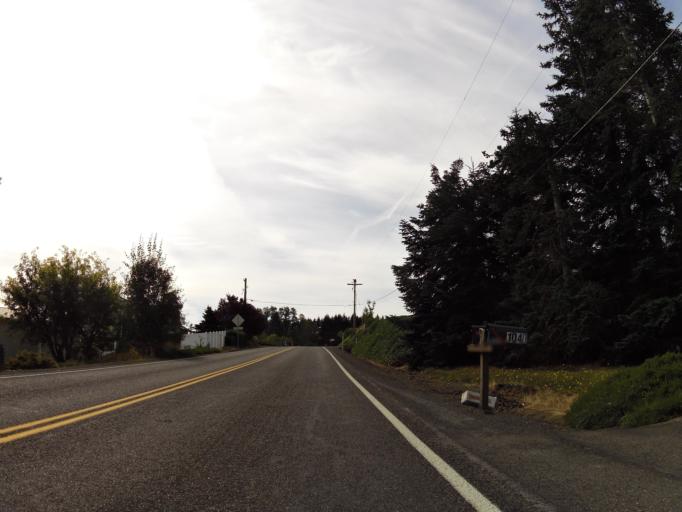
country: US
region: Washington
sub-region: Lewis County
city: Chehalis
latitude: 46.6264
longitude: -122.9674
